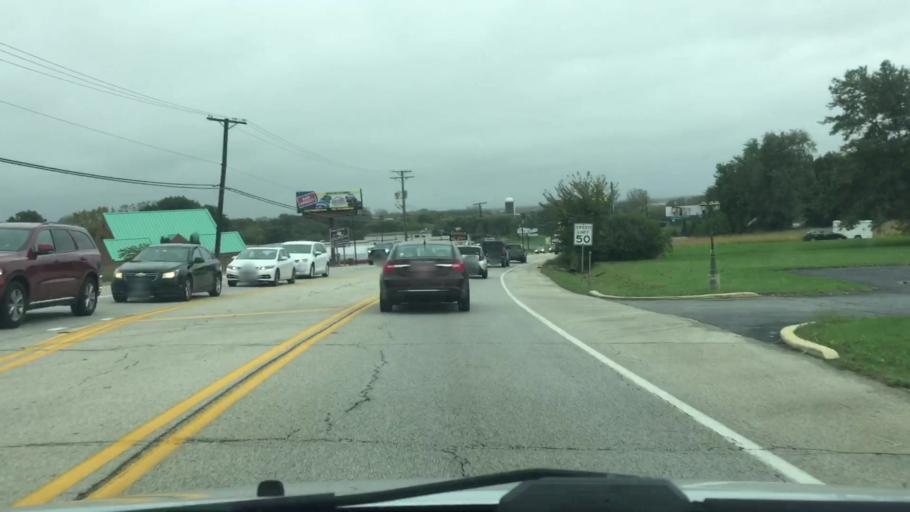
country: US
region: Illinois
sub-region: McHenry County
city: McCullom Lake
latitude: 42.3781
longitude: -88.2694
